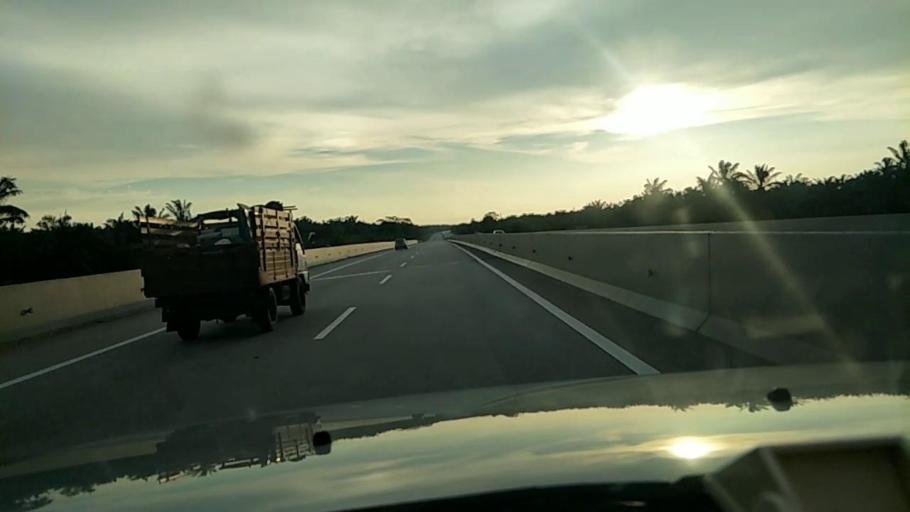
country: MY
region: Selangor
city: Batu Arang
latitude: 3.2886
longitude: 101.4311
